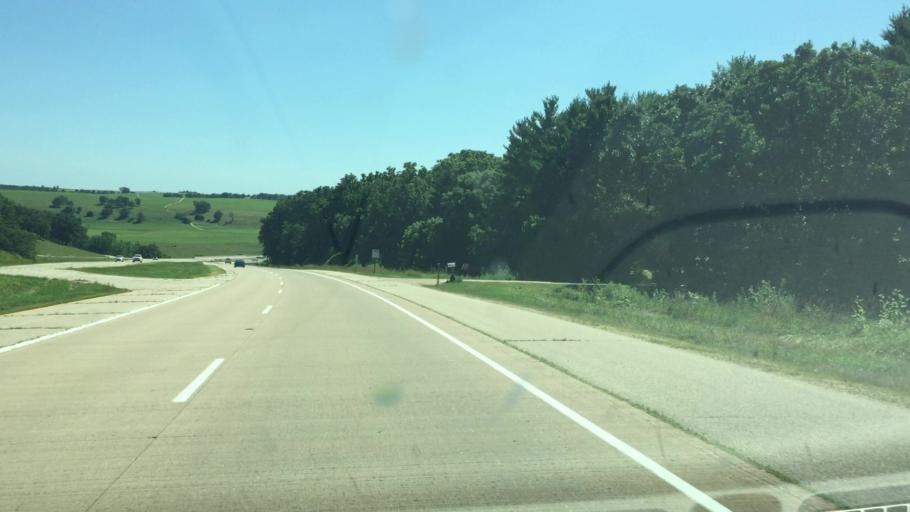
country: US
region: Wisconsin
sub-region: Iowa County
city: Mineral Point
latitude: 42.8172
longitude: -90.2569
